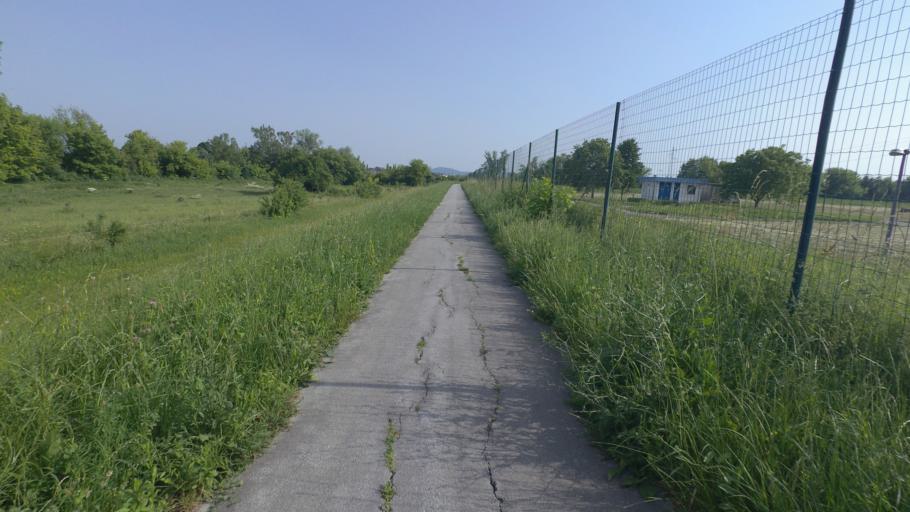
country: HR
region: Karlovacka
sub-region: Grad Karlovac
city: Karlovac
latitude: 45.4915
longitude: 15.5710
